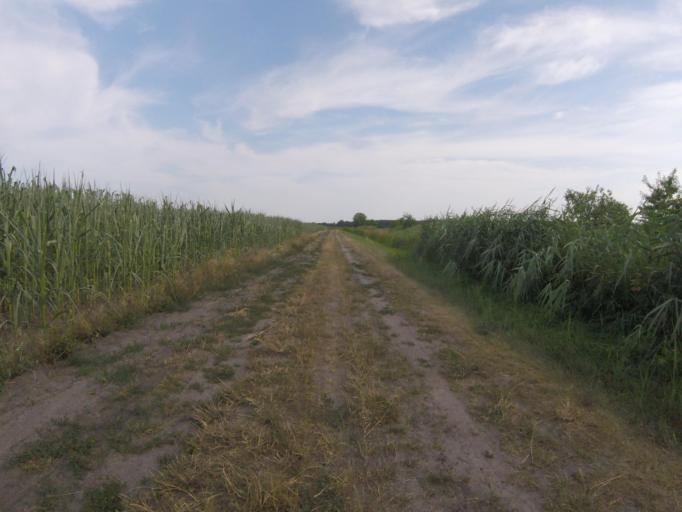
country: DE
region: Brandenburg
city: Spreenhagen
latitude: 52.2844
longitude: 13.8105
